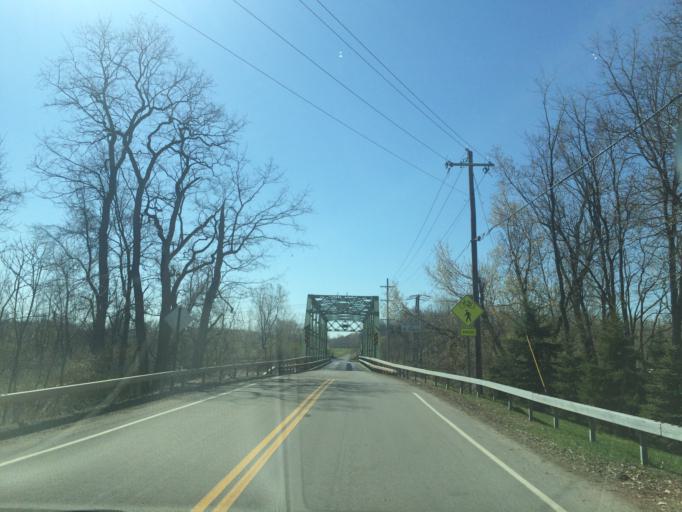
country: US
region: New York
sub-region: Wayne County
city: Palmyra
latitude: 43.0644
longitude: -77.2585
